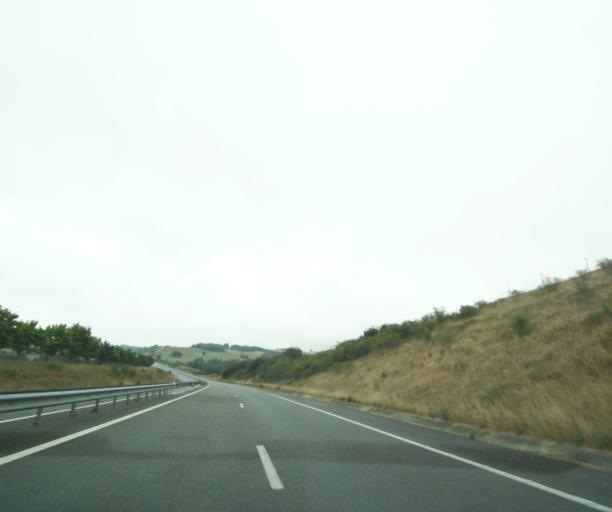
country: FR
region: Midi-Pyrenees
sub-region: Departement du Tarn
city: Carmaux
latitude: 44.0372
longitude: 2.2042
